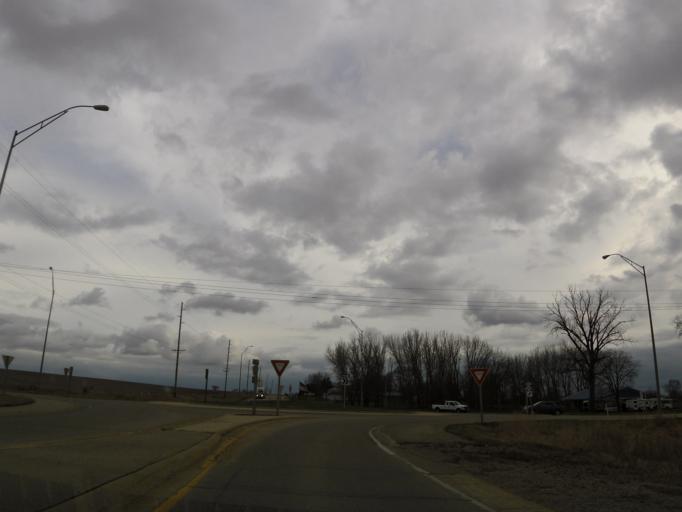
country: US
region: Iowa
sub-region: Black Hawk County
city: Elk Run Heights
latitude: 42.4983
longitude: -92.2197
